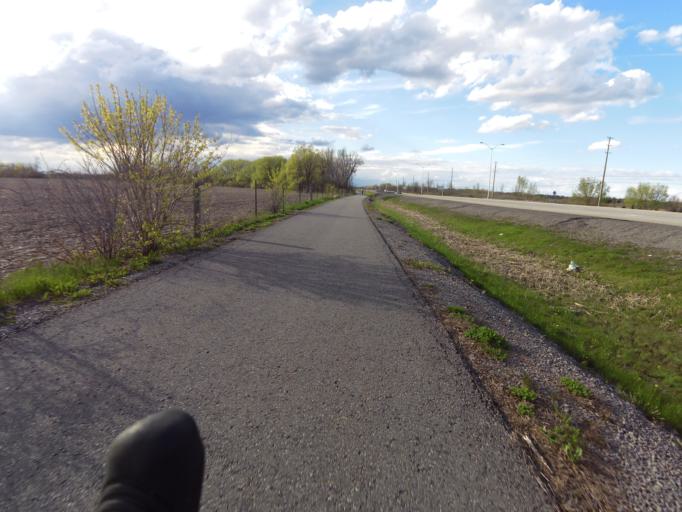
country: CA
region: Ontario
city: Ottawa
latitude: 45.2994
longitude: -75.6784
